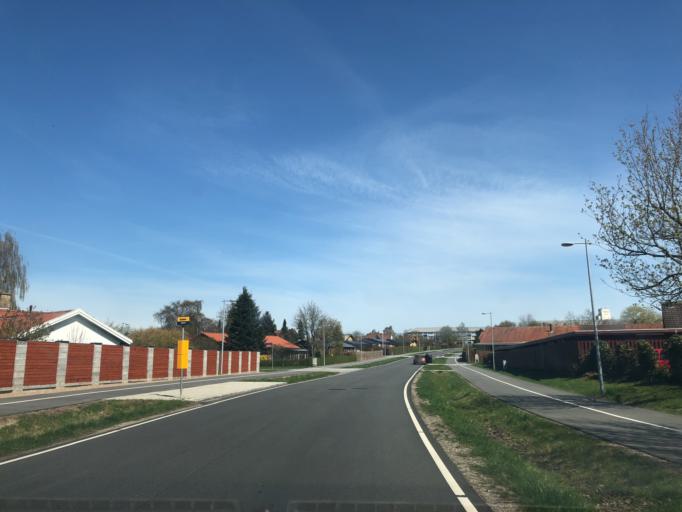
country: DK
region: Zealand
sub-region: Ringsted Kommune
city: Ringsted
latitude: 55.4313
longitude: 11.7841
